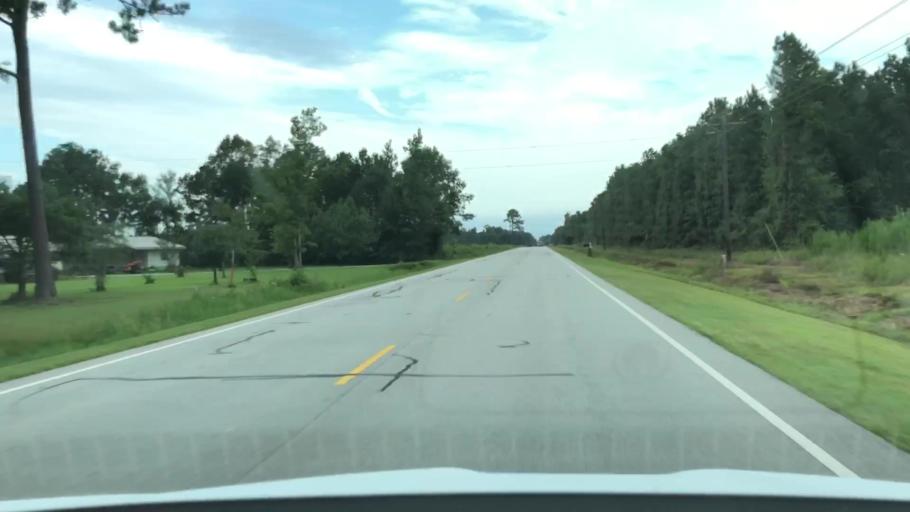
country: US
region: North Carolina
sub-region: Lenoir County
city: Kinston
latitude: 35.1245
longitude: -77.5197
